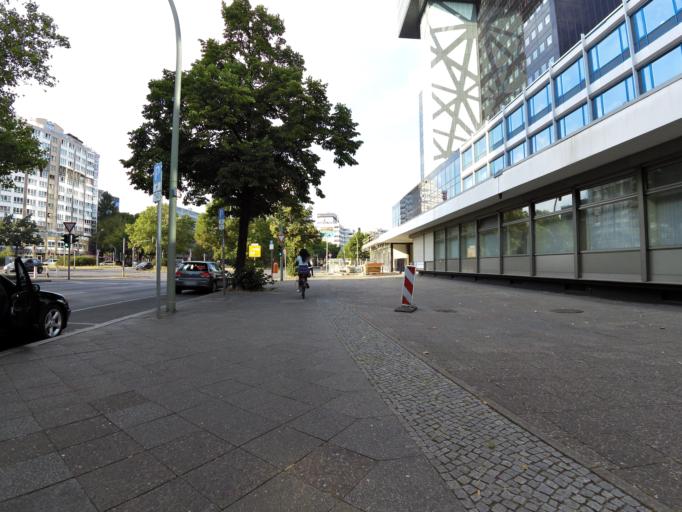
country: DE
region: Berlin
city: Berlin Schoeneberg
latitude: 52.4997
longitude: 13.3462
